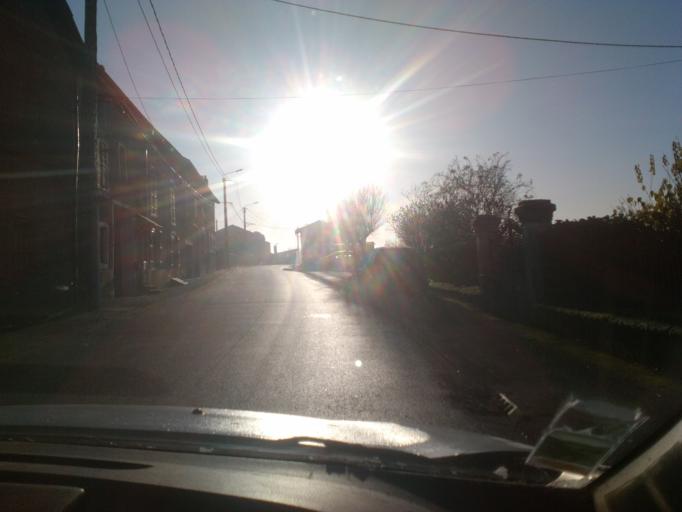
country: FR
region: Lorraine
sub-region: Departement des Vosges
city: Darnieulles
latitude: 48.1783
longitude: 6.2118
